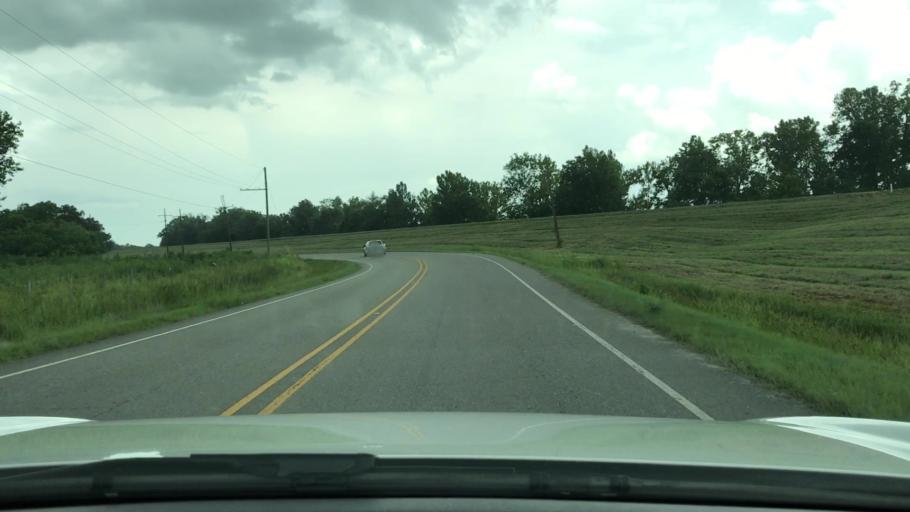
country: US
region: Louisiana
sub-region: Iberville Parish
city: Plaquemine
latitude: 30.2749
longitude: -91.2083
